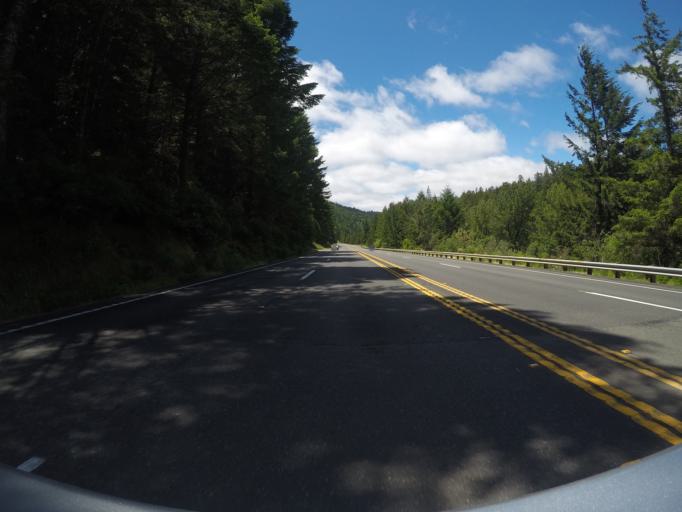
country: US
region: California
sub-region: Humboldt County
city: Redway
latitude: 40.2562
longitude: -123.8374
